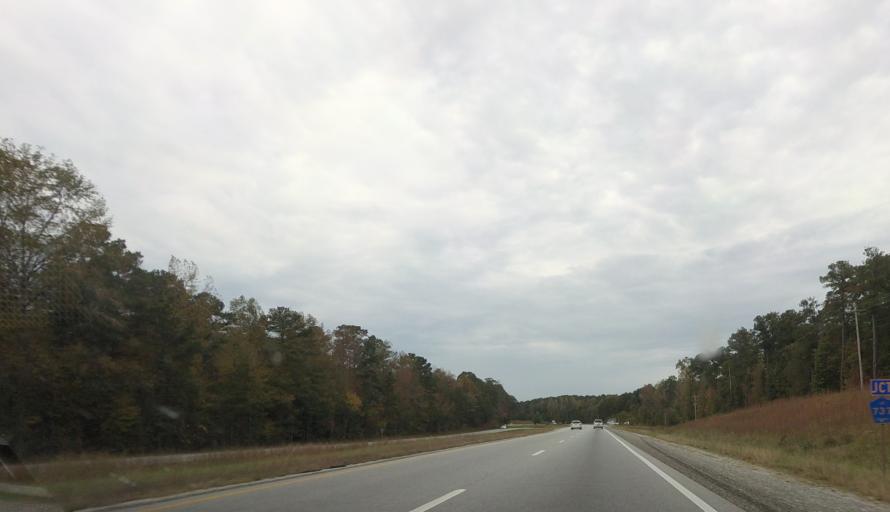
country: US
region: Alabama
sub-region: Lee County
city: Opelika
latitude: 32.6312
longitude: -85.2839
